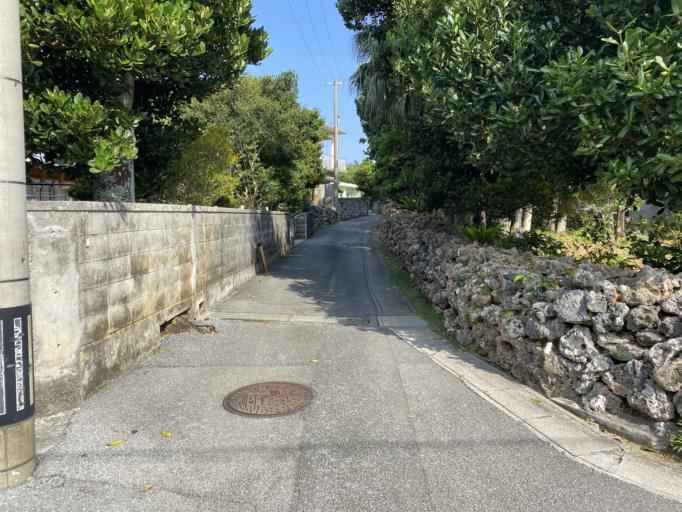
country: JP
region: Okinawa
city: Ishigaki
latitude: 24.0607
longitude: 123.7766
